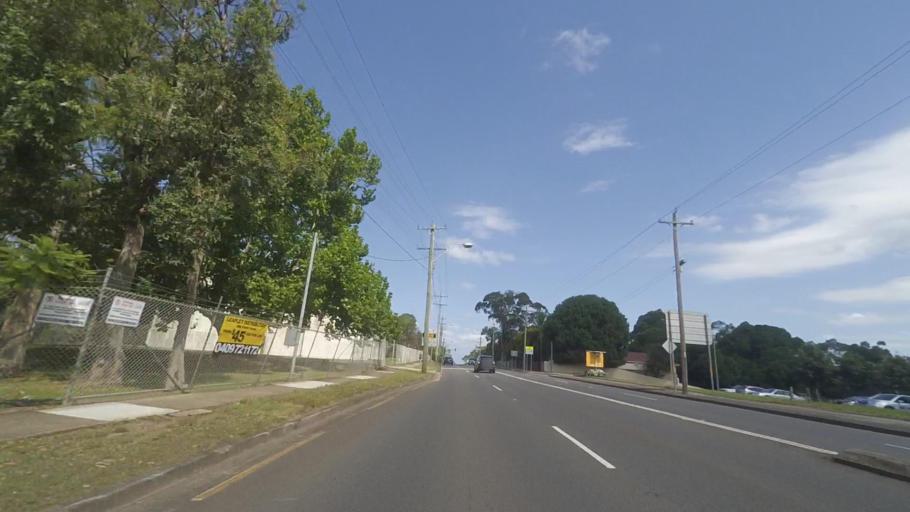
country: AU
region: New South Wales
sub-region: Parramatta
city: Carlingford
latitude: -33.7806
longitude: 151.0537
